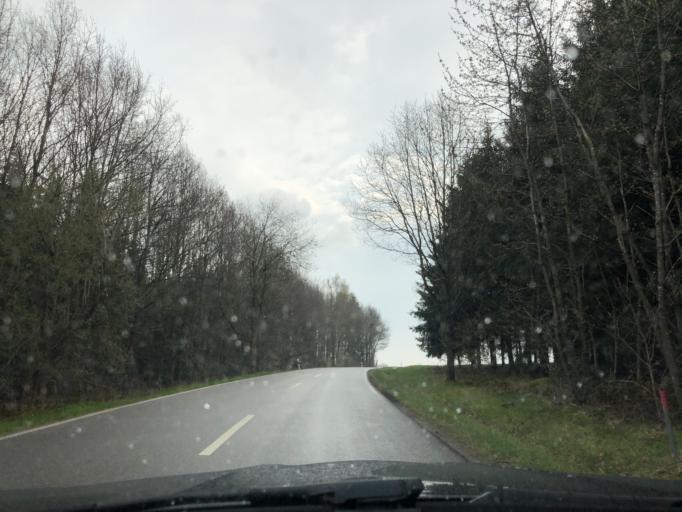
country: DE
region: Bavaria
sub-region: Upper Bavaria
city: Wolfersdorf
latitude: 48.4947
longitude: 11.6914
